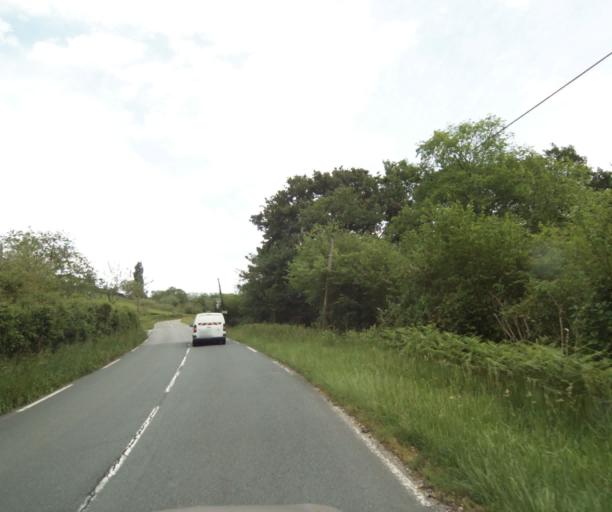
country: FR
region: Aquitaine
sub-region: Departement des Pyrenees-Atlantiques
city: Mouguerre
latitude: 43.4628
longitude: -1.4161
